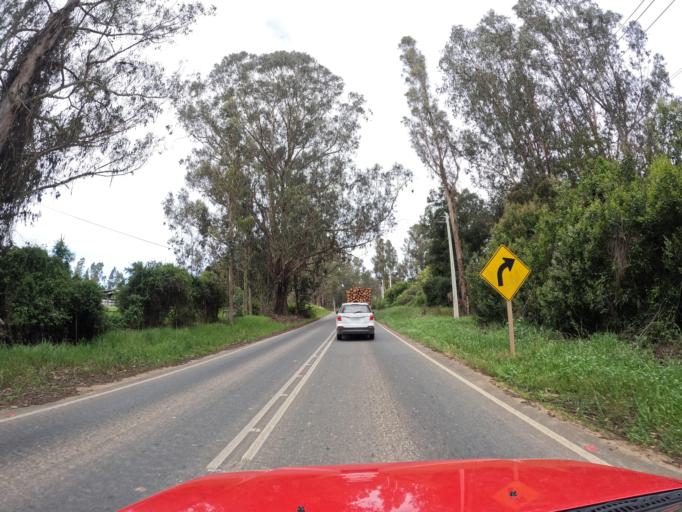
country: CL
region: O'Higgins
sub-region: Provincia de Colchagua
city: Santa Cruz
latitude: -34.3580
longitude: -71.8850
